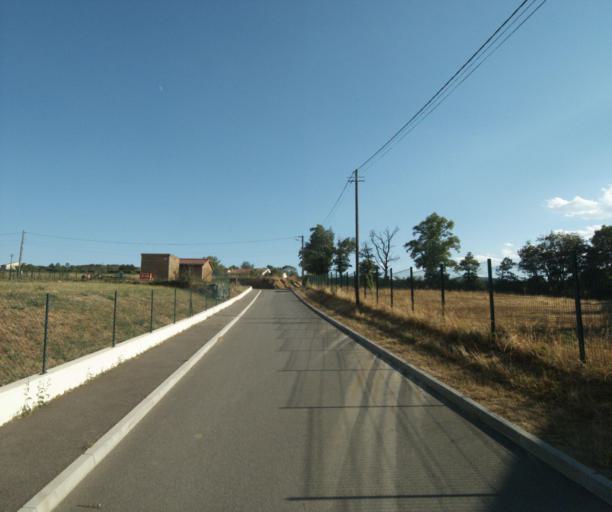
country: FR
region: Rhone-Alpes
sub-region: Departement du Rhone
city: Lentilly
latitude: 45.8158
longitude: 4.6669
